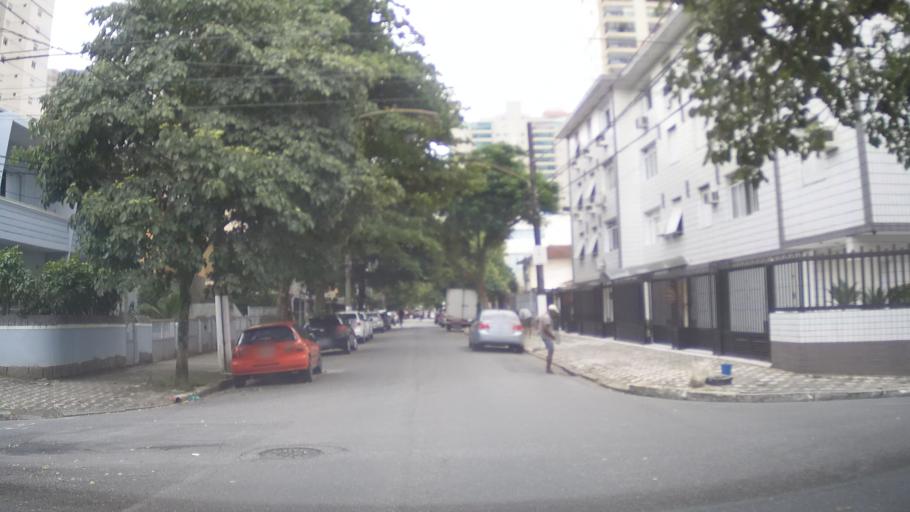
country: BR
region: Sao Paulo
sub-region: Santos
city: Santos
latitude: -23.9726
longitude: -46.3155
